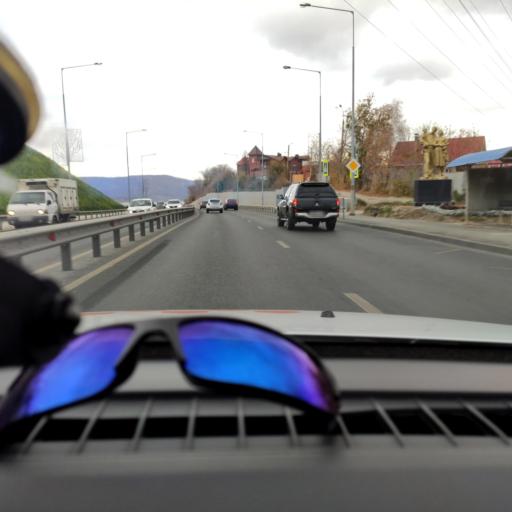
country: RU
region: Samara
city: Volzhskiy
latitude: 53.3701
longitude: 50.1886
